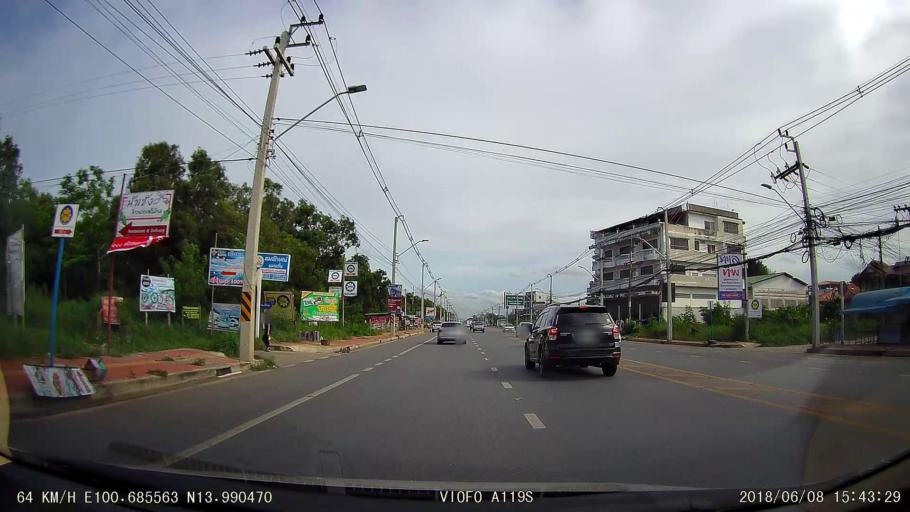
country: TH
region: Pathum Thani
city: Thanyaburi
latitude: 13.9903
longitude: 100.6856
